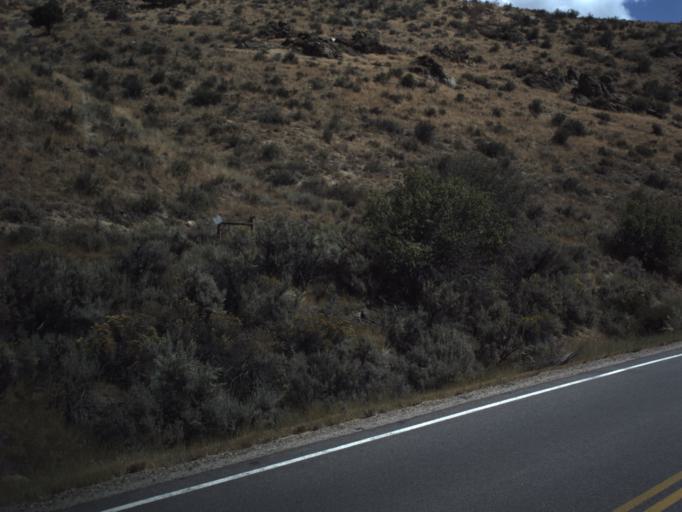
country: US
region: Utah
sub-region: Rich County
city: Randolph
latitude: 41.8203
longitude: -111.2845
